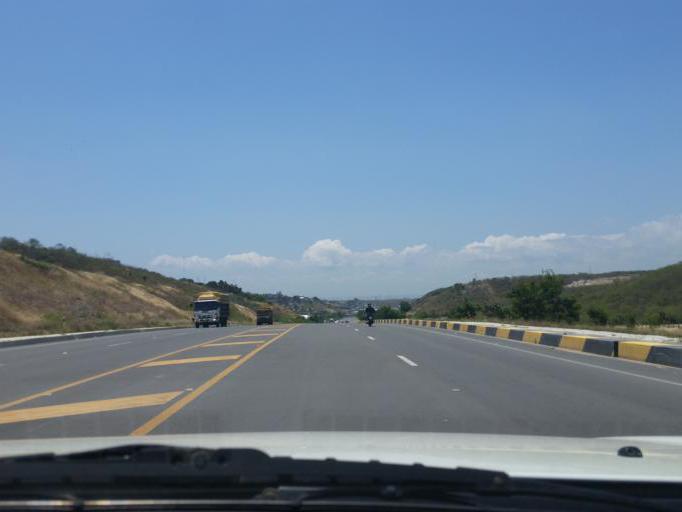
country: EC
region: Manabi
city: Manta
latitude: -0.9610
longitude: -80.7515
